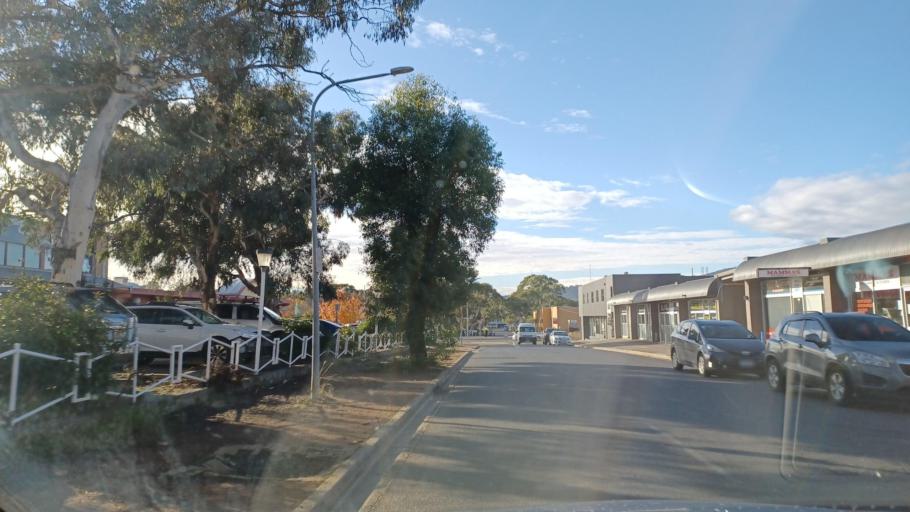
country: AU
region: Australian Capital Territory
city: Kaleen
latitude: -35.2181
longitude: 149.1398
